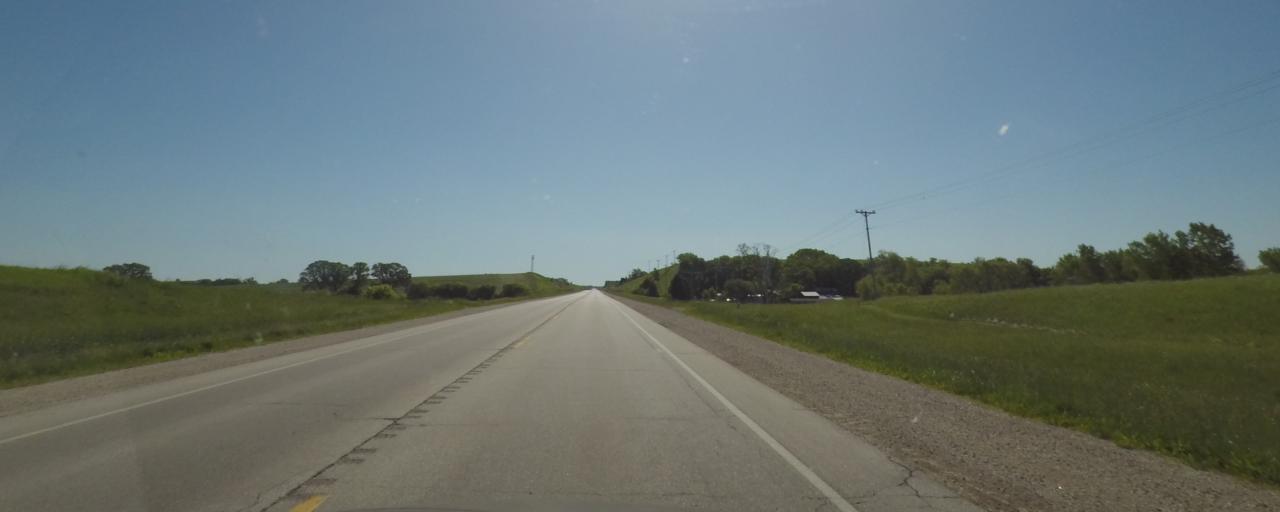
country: US
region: Wisconsin
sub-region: Fond du Lac County
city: Saint Peter
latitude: 43.7833
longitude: -88.3209
